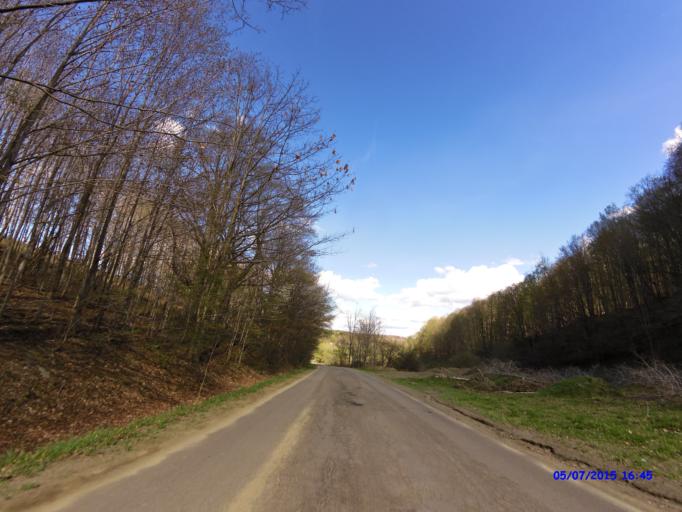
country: US
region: New York
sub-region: Cattaraugus County
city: Little Valley
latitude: 42.2844
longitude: -78.7134
